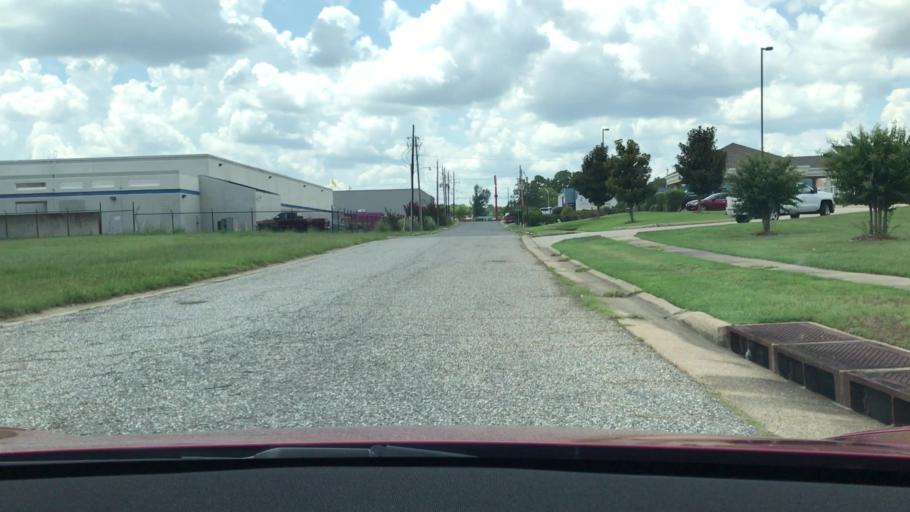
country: US
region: Louisiana
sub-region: De Soto Parish
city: Stonewall
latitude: 32.3980
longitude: -93.8047
